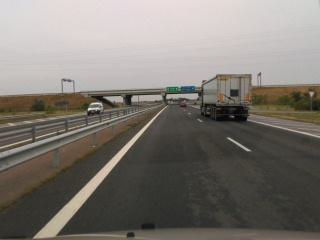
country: BG
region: Stara Zagora
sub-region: Obshtina Stara Zagora
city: Stara Zagora
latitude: 42.3388
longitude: 25.6600
